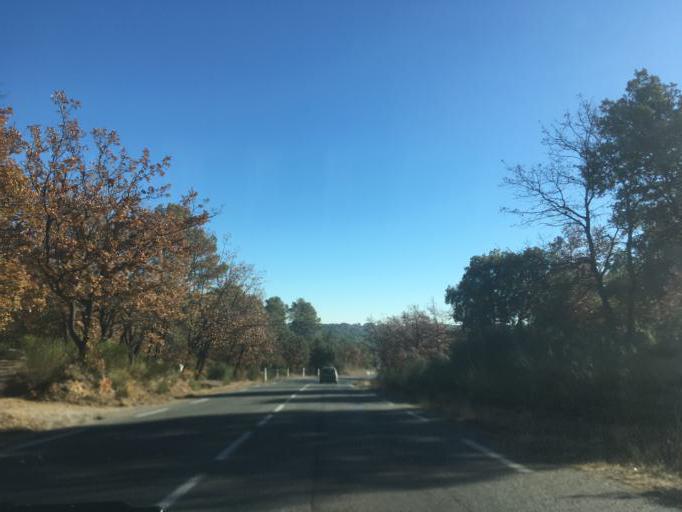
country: FR
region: Provence-Alpes-Cote d'Azur
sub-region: Departement du Var
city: Flayosc
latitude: 43.5450
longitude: 6.3421
